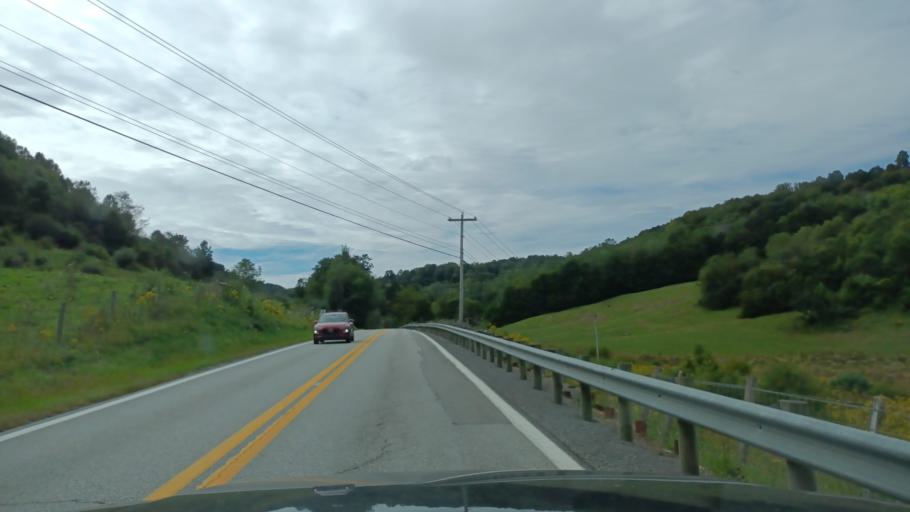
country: US
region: West Virginia
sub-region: Taylor County
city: Grafton
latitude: 39.3291
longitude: -80.1100
